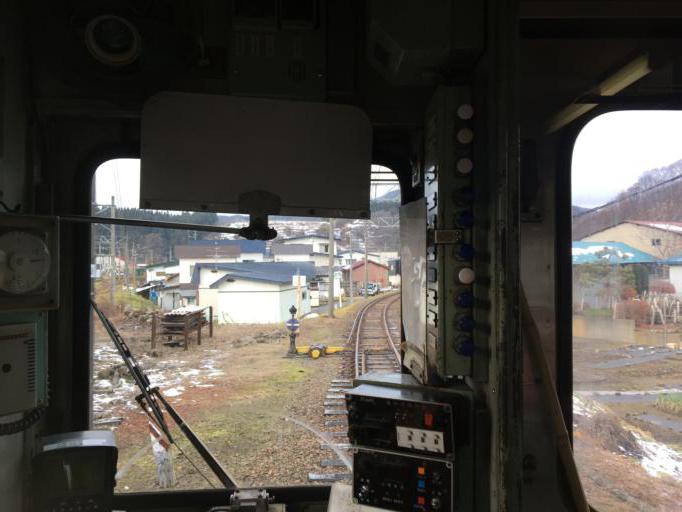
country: JP
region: Aomori
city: Hirosaki
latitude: 40.5217
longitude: 140.5657
